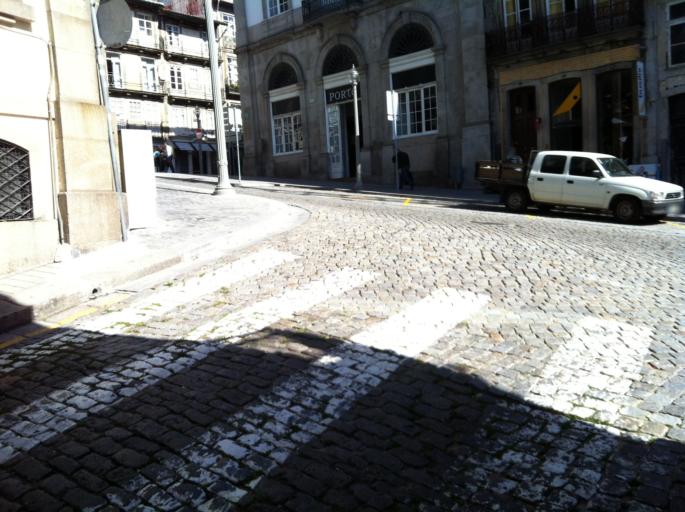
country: PT
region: Porto
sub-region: Porto
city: Porto
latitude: 41.1425
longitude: -8.6155
